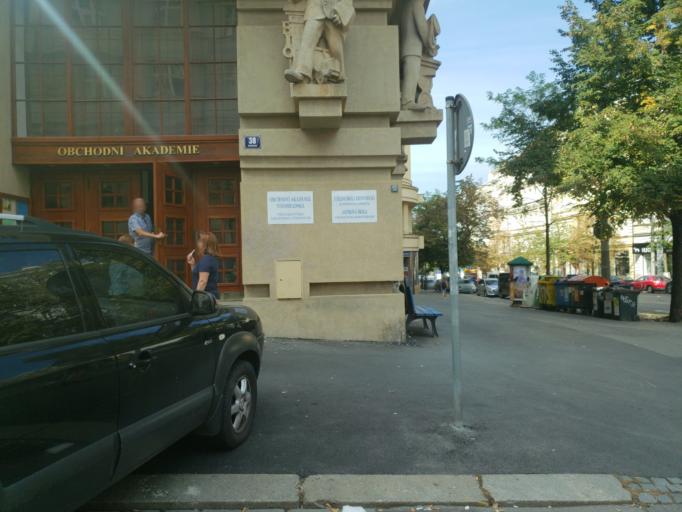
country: CZ
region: Praha
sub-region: Praha 8
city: Karlin
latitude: 50.0773
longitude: 14.4393
